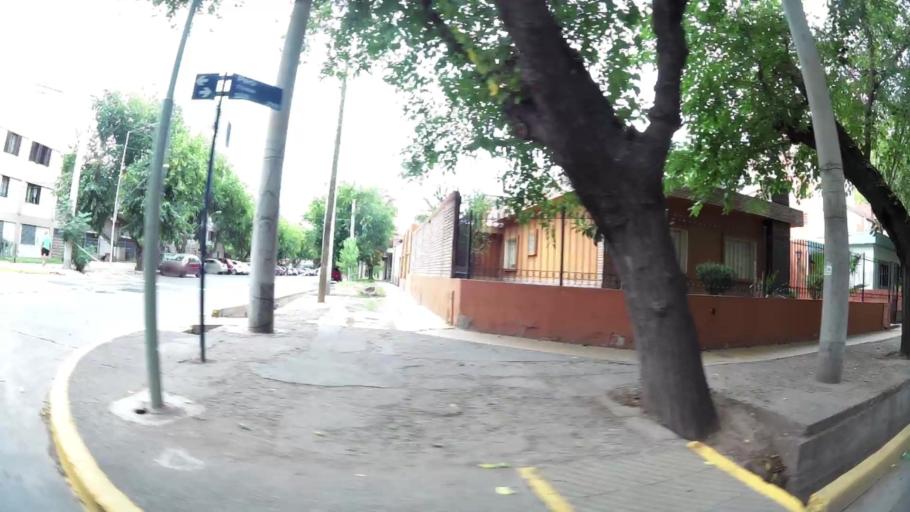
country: AR
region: Mendoza
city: Mendoza
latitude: -32.8760
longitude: -68.8449
